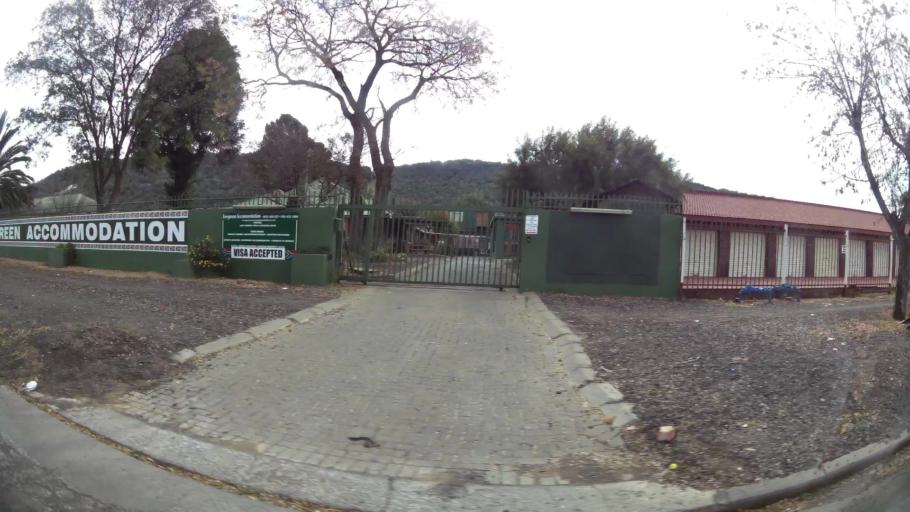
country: ZA
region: Orange Free State
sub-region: Mangaung Metropolitan Municipality
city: Bloemfontein
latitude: -29.0994
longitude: 26.2429
